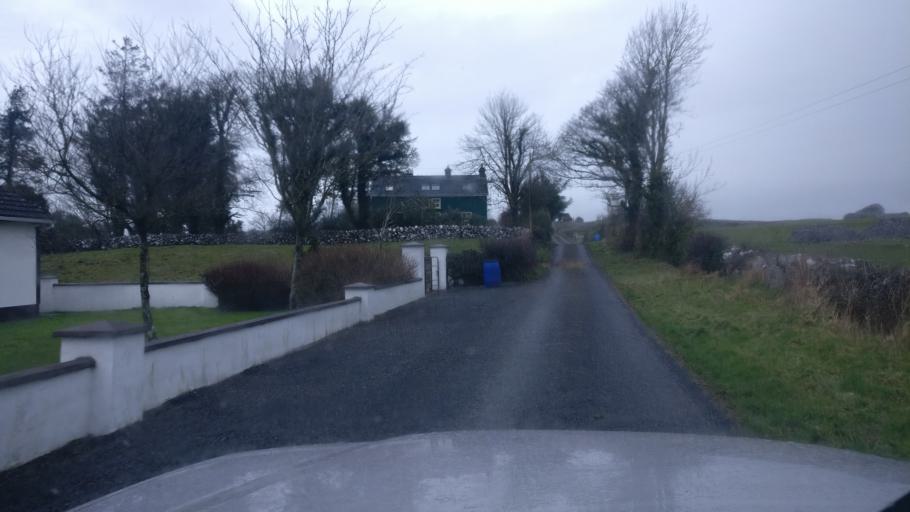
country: IE
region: Connaught
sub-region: County Galway
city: Loughrea
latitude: 53.1907
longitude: -8.6791
